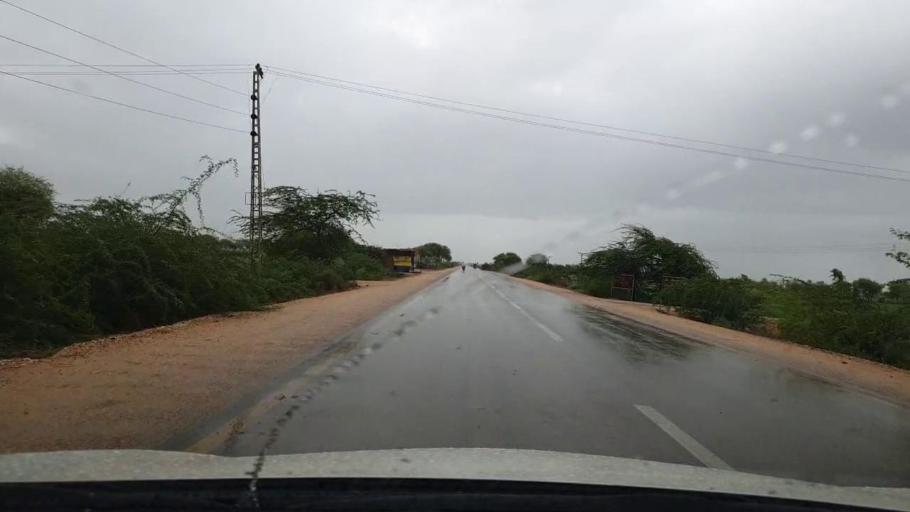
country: PK
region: Sindh
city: Kario
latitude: 24.6533
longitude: 68.5796
